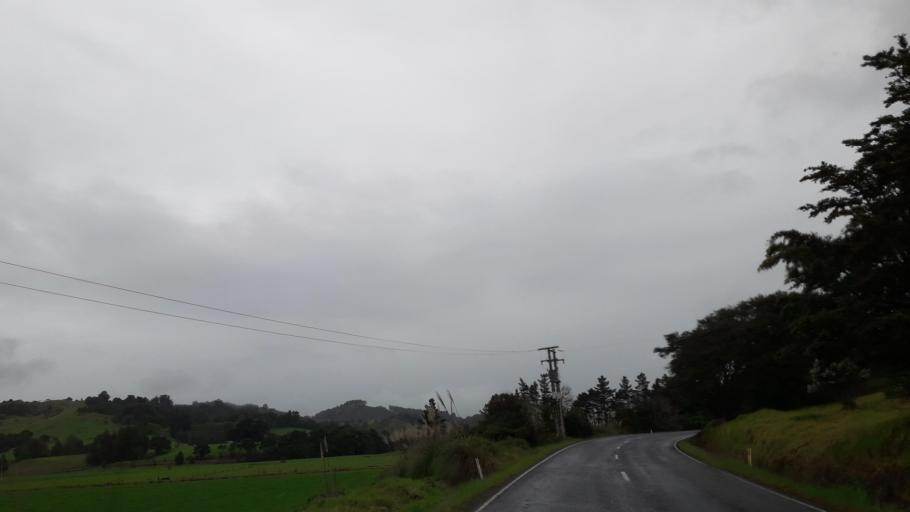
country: NZ
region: Northland
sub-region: Far North District
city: Kaitaia
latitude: -35.3609
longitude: 173.4945
